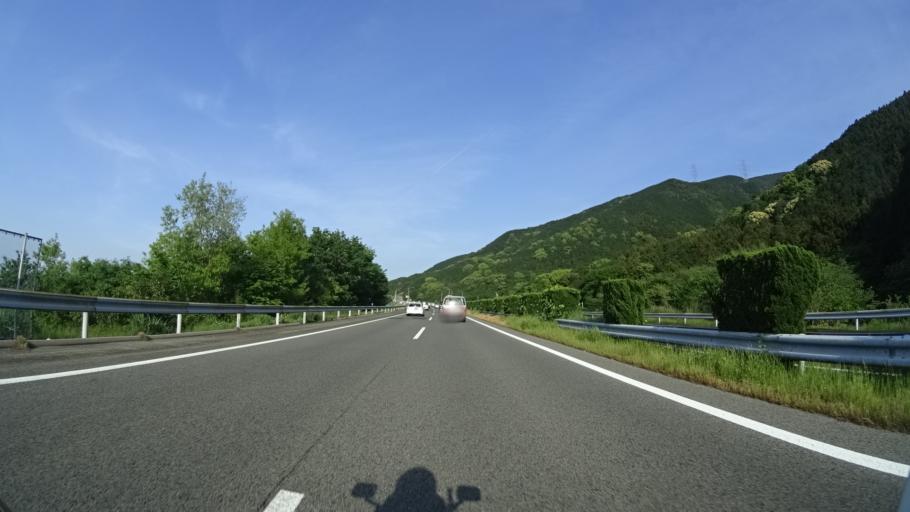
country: JP
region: Ehime
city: Kawanoecho
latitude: 33.9556
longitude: 133.4642
